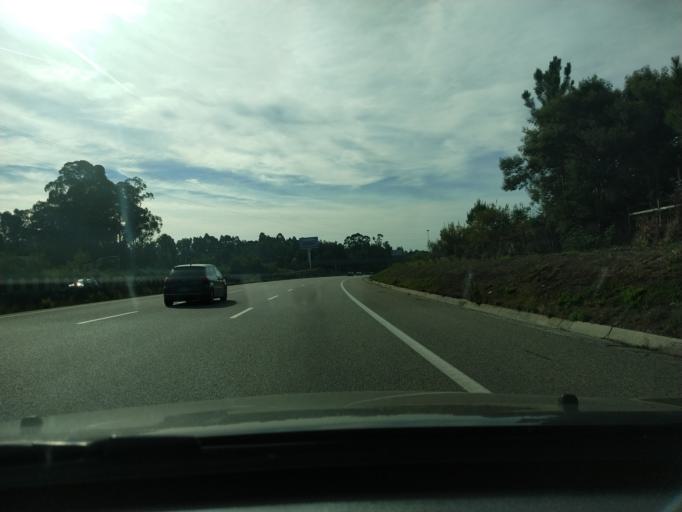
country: PT
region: Aveiro
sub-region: Santa Maria da Feira
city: Rio Meao
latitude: 40.9661
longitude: -8.5684
